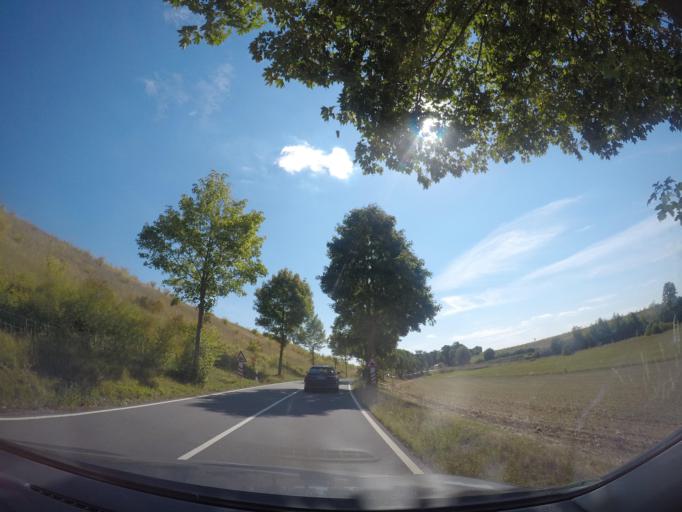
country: DE
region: Lower Saxony
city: Bad Lauterberg im Harz
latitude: 51.6050
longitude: 10.4733
